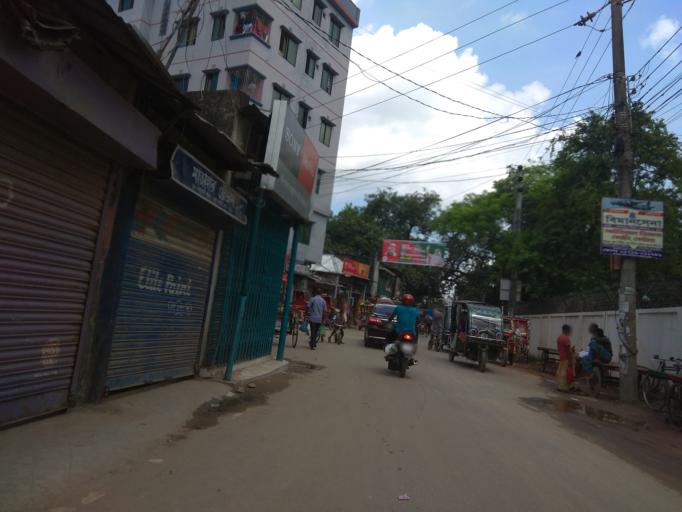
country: BD
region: Dhaka
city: Tungi
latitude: 23.8291
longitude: 90.3916
